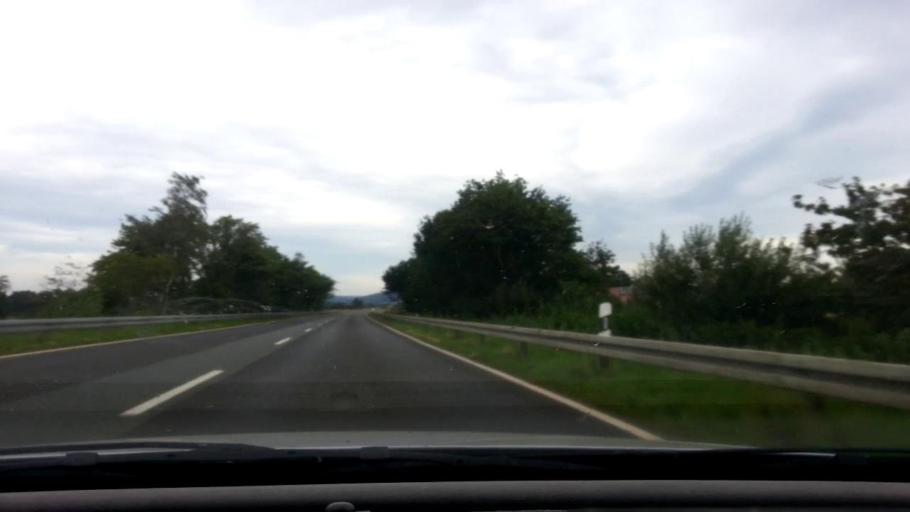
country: DE
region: Bavaria
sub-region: Upper Palatinate
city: Immenreuth
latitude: 49.8895
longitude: 11.8807
